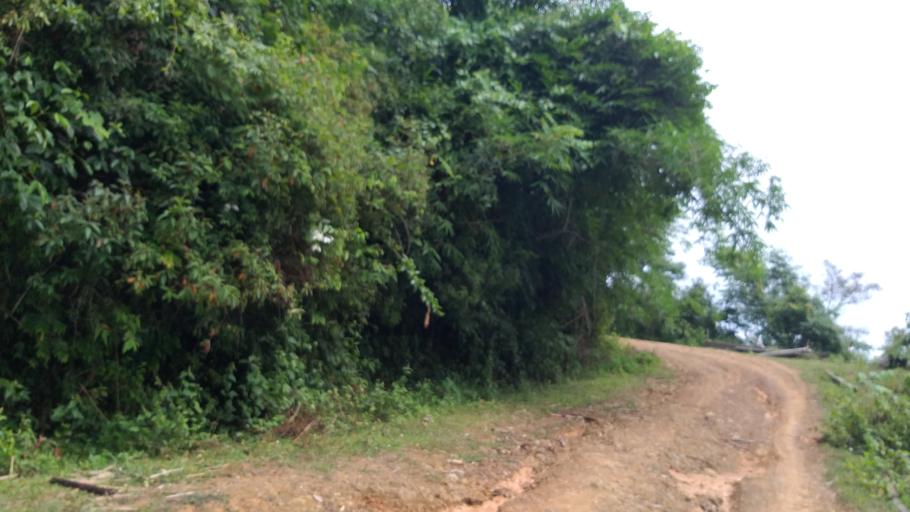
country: LA
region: Phongsali
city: Khoa
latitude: 21.3883
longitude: 102.6609
